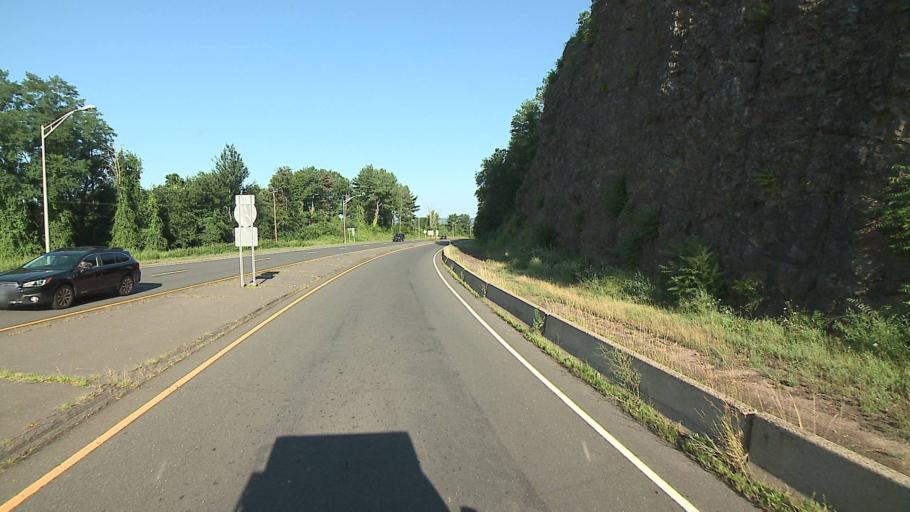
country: US
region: Connecticut
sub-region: Hartford County
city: Farmington
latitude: 41.7239
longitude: -72.8111
